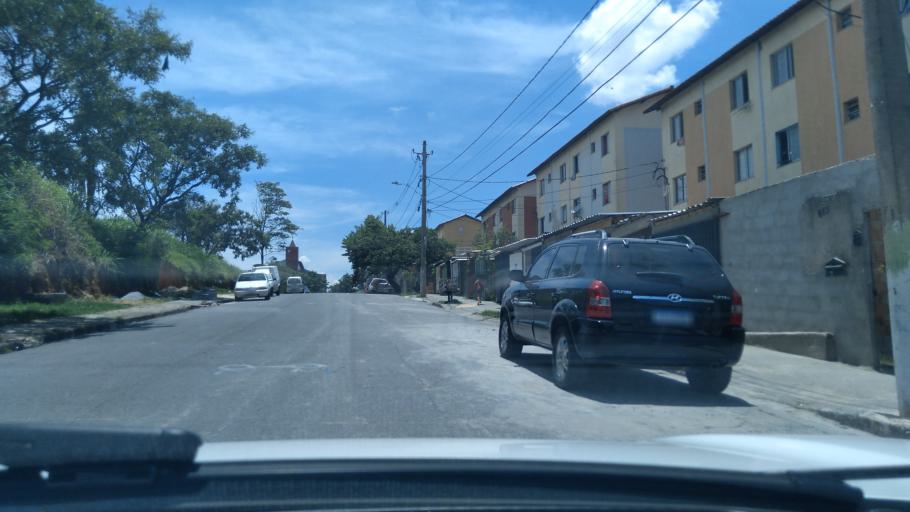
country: BR
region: Minas Gerais
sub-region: Contagem
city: Contagem
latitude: -19.9266
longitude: -44.0171
